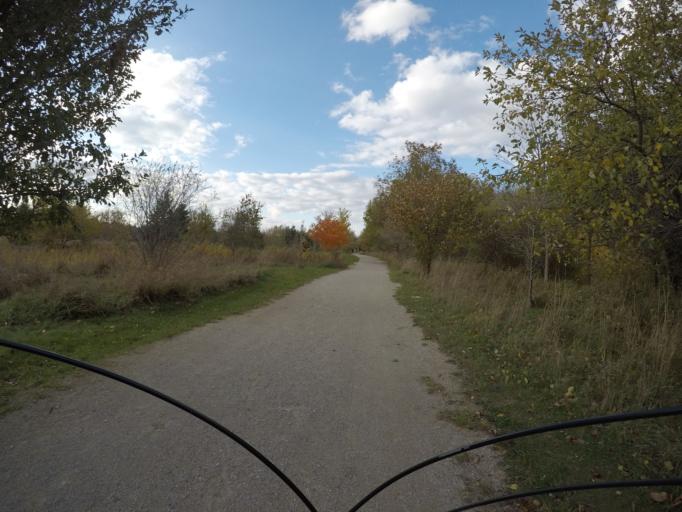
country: CA
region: Ontario
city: Waterloo
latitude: 43.5371
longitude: -80.5480
